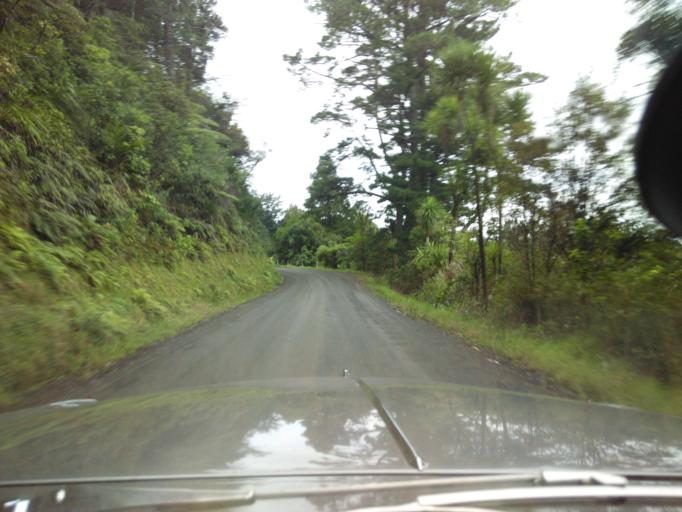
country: NZ
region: Auckland
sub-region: Auckland
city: Warkworth
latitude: -36.5303
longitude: 174.6416
